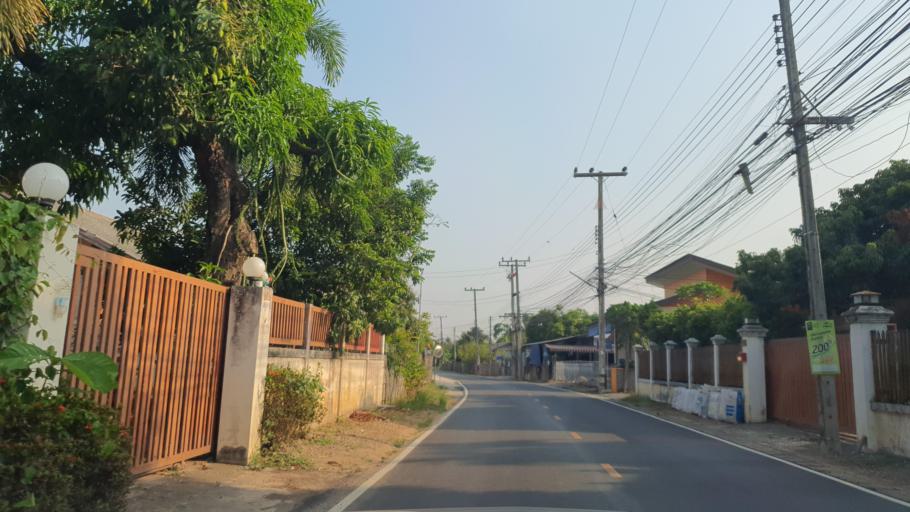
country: TH
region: Chiang Mai
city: Mae Wang
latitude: 18.6047
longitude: 98.8206
